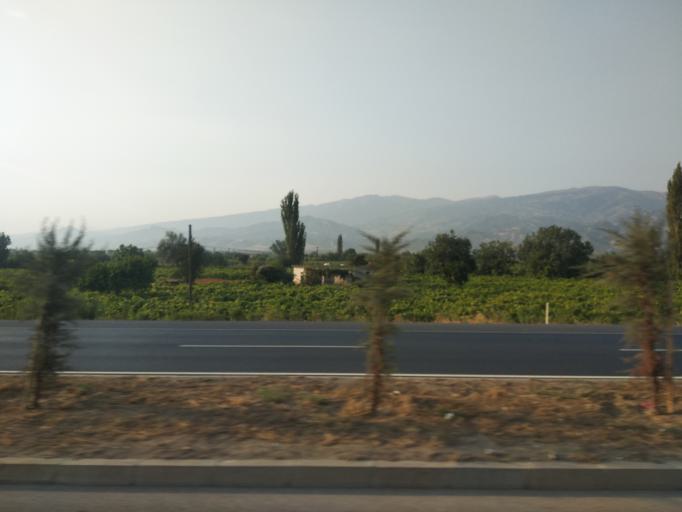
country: TR
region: Manisa
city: Salihli
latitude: 38.4968
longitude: 28.1889
